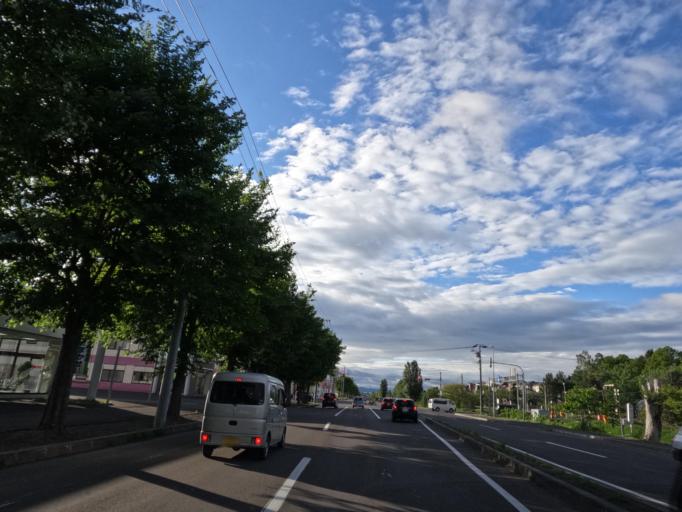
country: JP
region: Hokkaido
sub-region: Asahikawa-shi
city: Asahikawa
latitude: 43.7299
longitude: 142.3659
